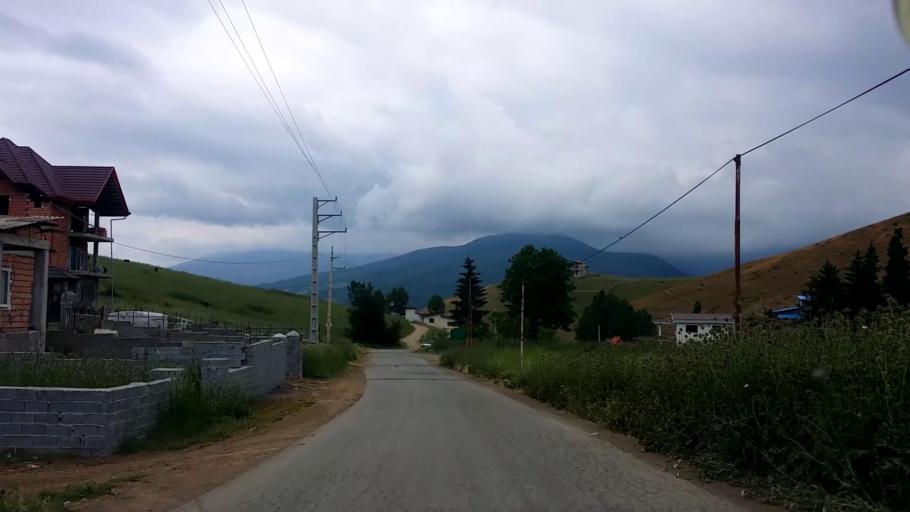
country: IR
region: Mazandaran
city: Chalus
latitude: 36.5226
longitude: 51.2620
